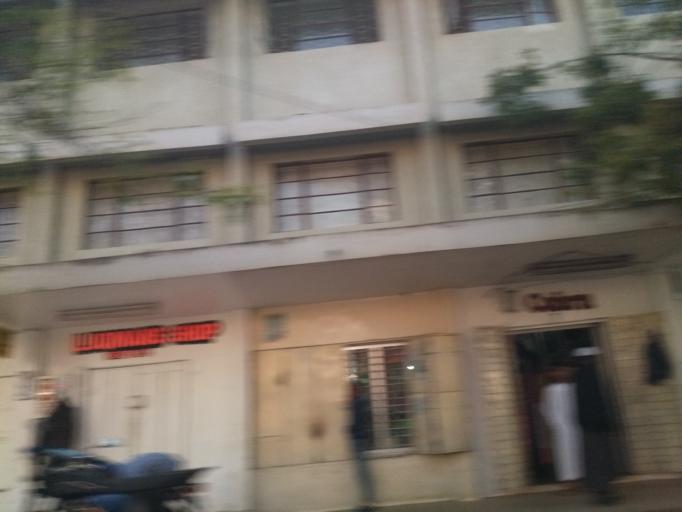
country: TZ
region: Arusha
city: Arusha
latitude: -3.3714
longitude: 36.6876
